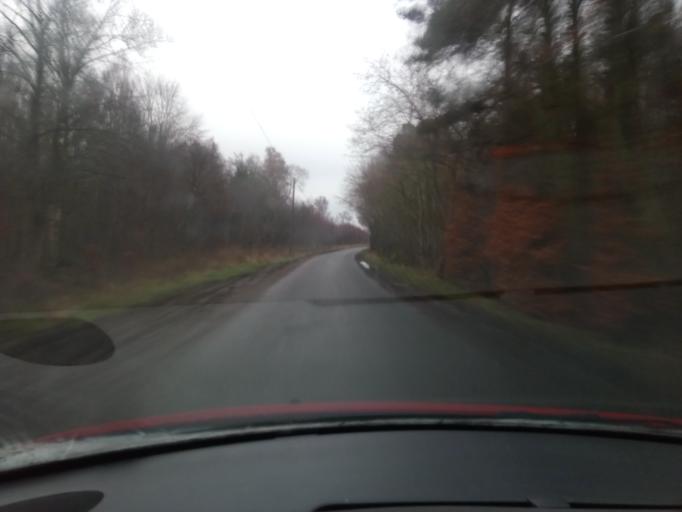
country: GB
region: Scotland
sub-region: The Scottish Borders
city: Kelso
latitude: 55.5542
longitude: -2.4308
